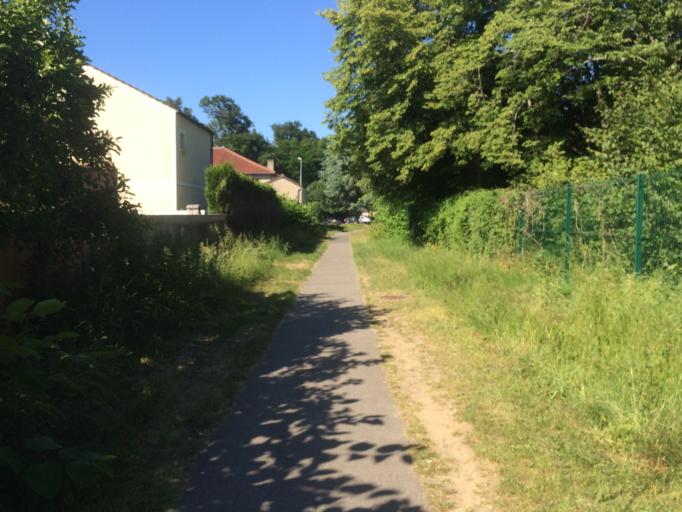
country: FR
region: Ile-de-France
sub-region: Departement du Val-de-Marne
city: Boissy-Saint-Leger
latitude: 48.7525
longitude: 2.5217
